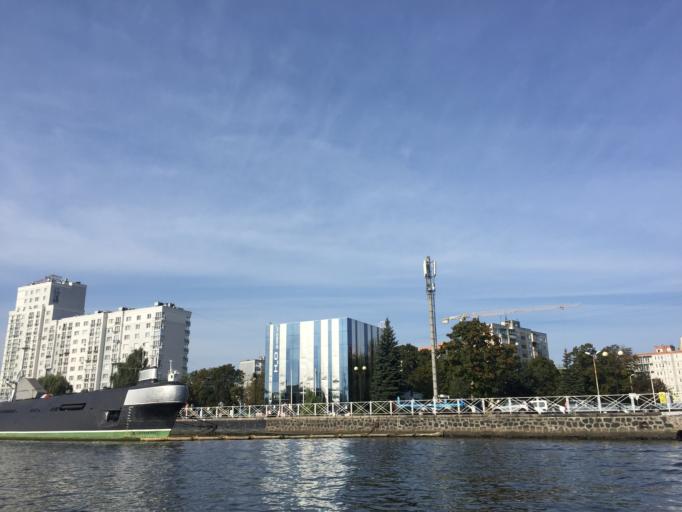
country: RU
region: Kaliningrad
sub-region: Gorod Kaliningrad
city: Kaliningrad
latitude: 54.7064
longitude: 20.4949
